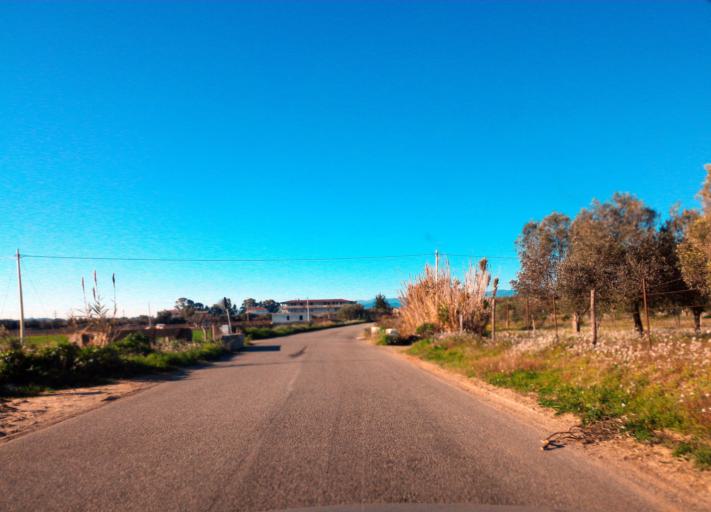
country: IT
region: Calabria
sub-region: Provincia di Crotone
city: Tronca
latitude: 39.2048
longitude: 17.1044
